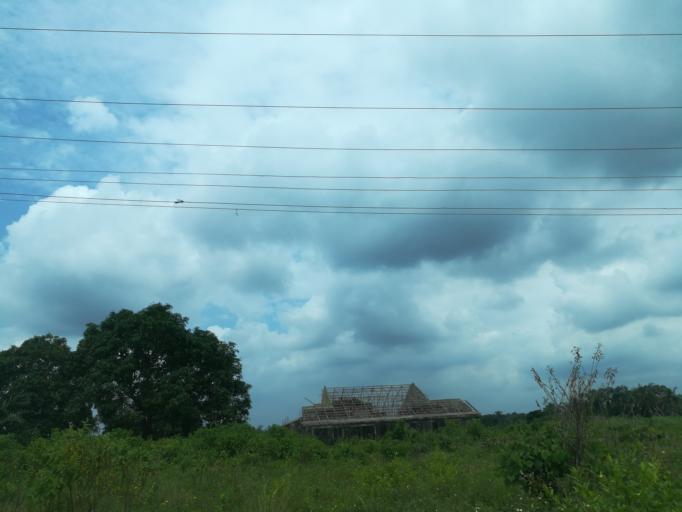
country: NG
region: Lagos
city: Ejirin
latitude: 6.6295
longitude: 3.7078
